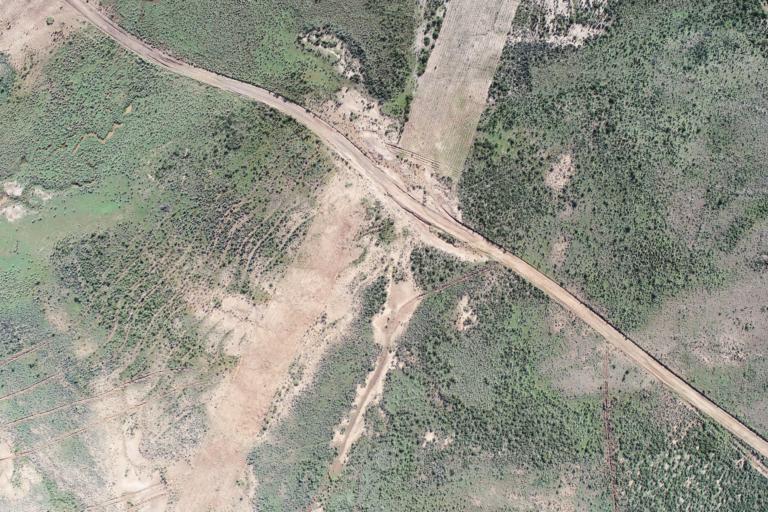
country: BO
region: La Paz
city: Curahuara de Carangas
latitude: -17.3023
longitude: -68.5041
